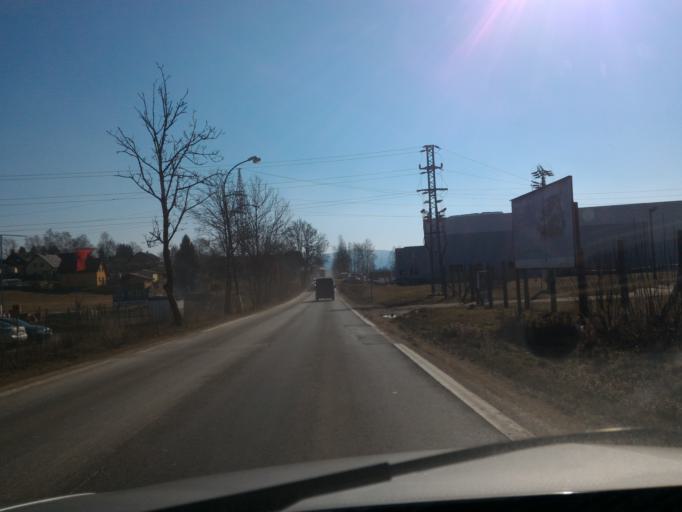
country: CZ
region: Liberecky
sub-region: Okres Jablonec nad Nisou
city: Jablonec nad Nisou
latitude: 50.7465
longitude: 15.1377
